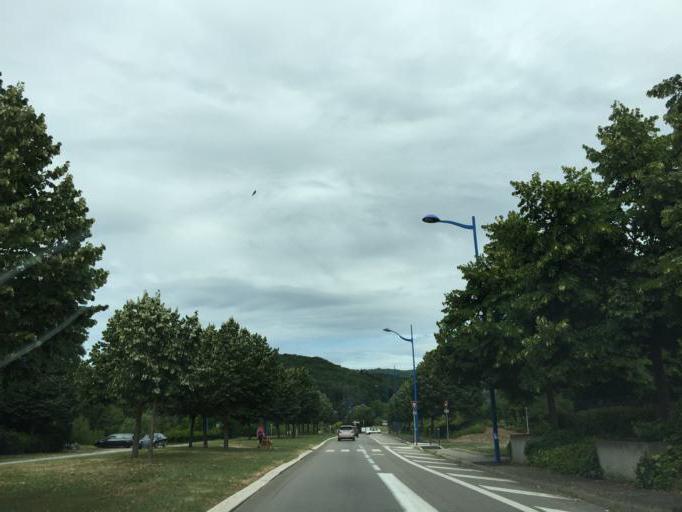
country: FR
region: Rhone-Alpes
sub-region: Departement de la Loire
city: Unieux
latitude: 45.3946
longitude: 4.2646
